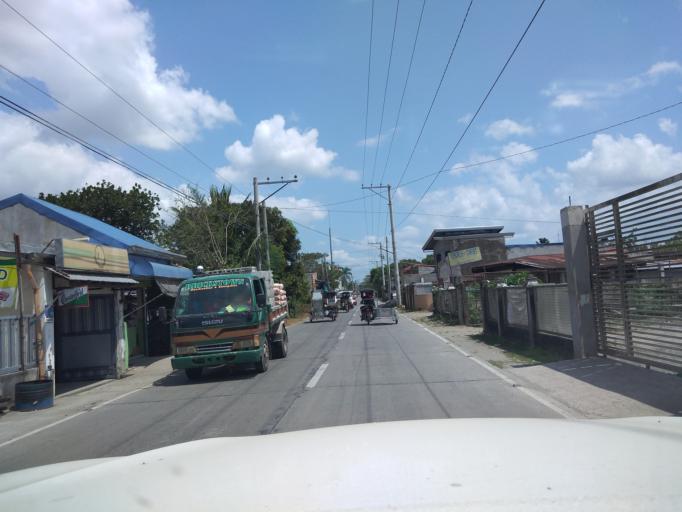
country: PH
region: Central Luzon
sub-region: Province of Pampanga
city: Lourdes
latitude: 15.0192
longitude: 120.8586
